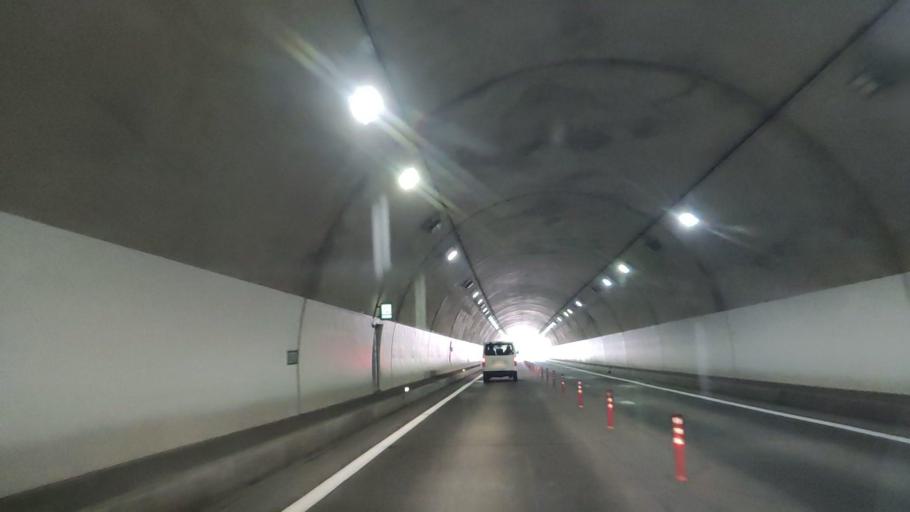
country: JP
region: Akita
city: Odate
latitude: 40.3242
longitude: 140.6006
